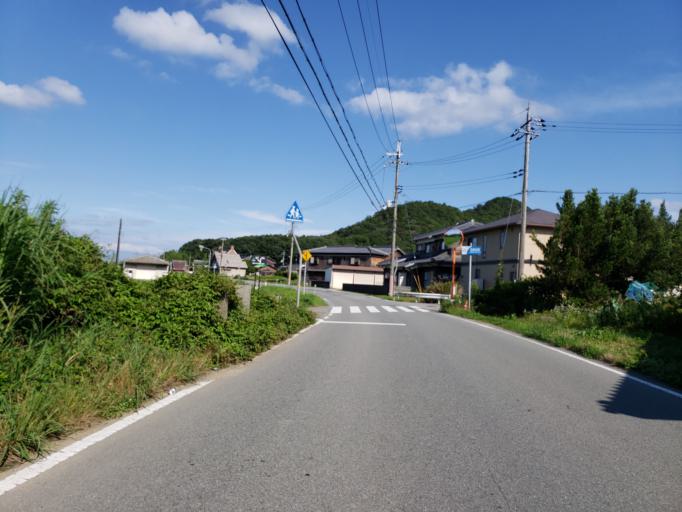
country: JP
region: Hyogo
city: Kakogawacho-honmachi
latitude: 34.8957
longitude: 134.8034
